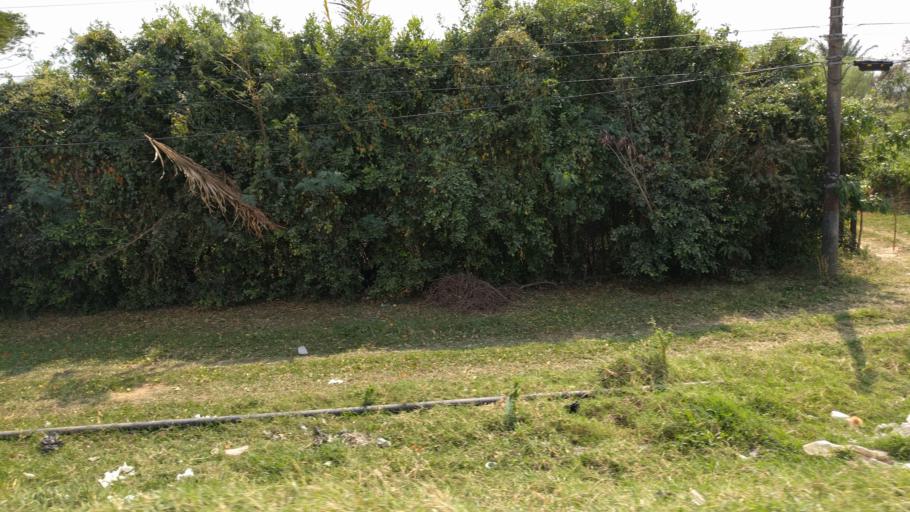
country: BO
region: Santa Cruz
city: Santiago del Torno
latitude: -17.9770
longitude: -63.3682
